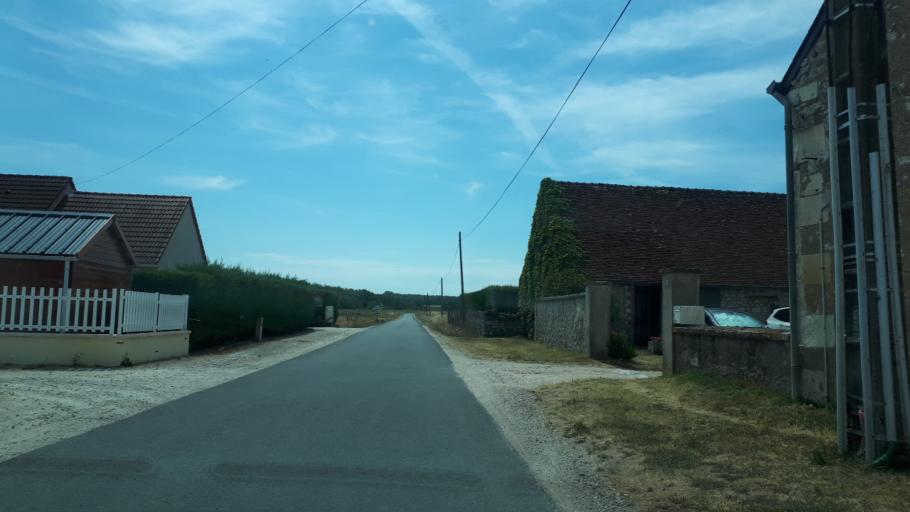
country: FR
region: Centre
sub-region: Departement du Loir-et-Cher
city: Chitenay
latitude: 47.4360
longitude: 1.3544
